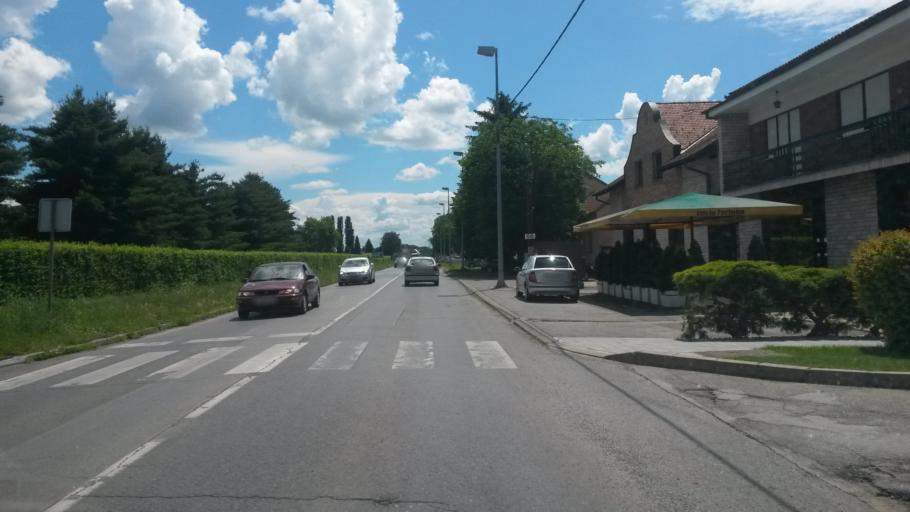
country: HR
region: Osjecko-Baranjska
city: Viskovci
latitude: 45.3274
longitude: 18.4184
